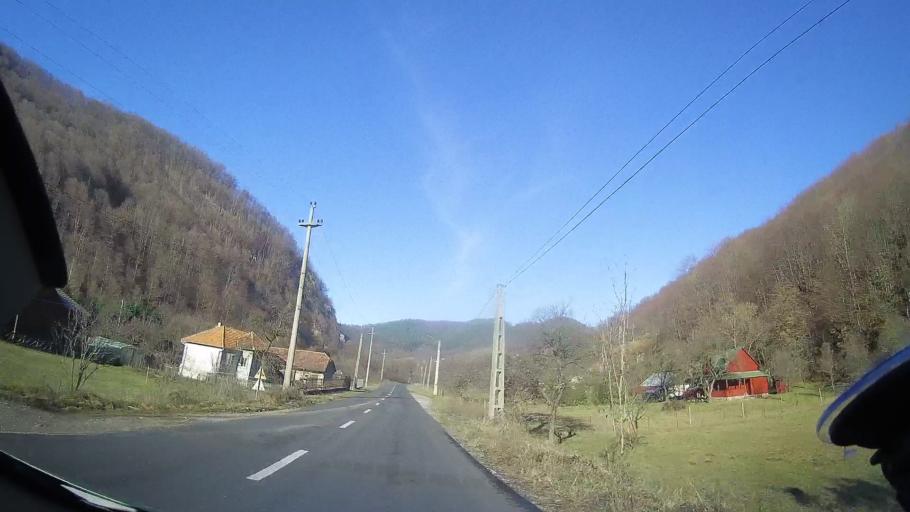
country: RO
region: Bihor
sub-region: Comuna Bulz
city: Bulz
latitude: 46.9177
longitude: 22.6555
